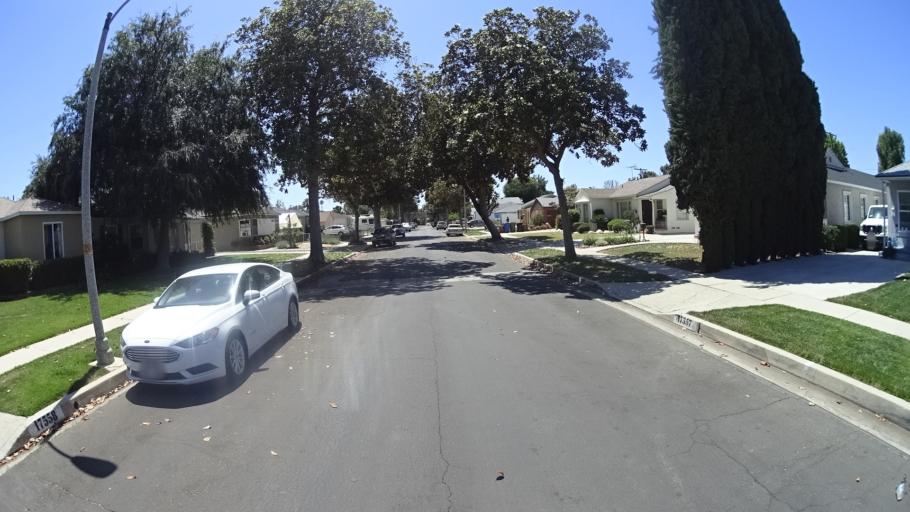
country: US
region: California
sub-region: Los Angeles County
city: Northridge
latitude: 34.1911
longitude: -118.5163
